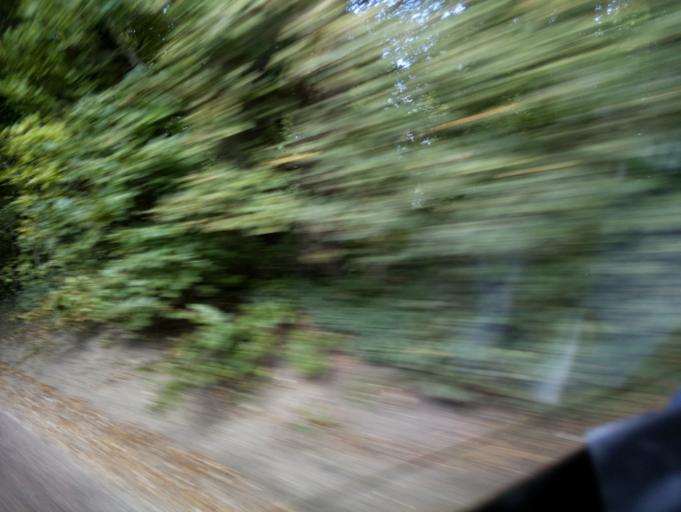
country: GB
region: England
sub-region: Hampshire
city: Basingstoke
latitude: 51.2313
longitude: -1.0657
